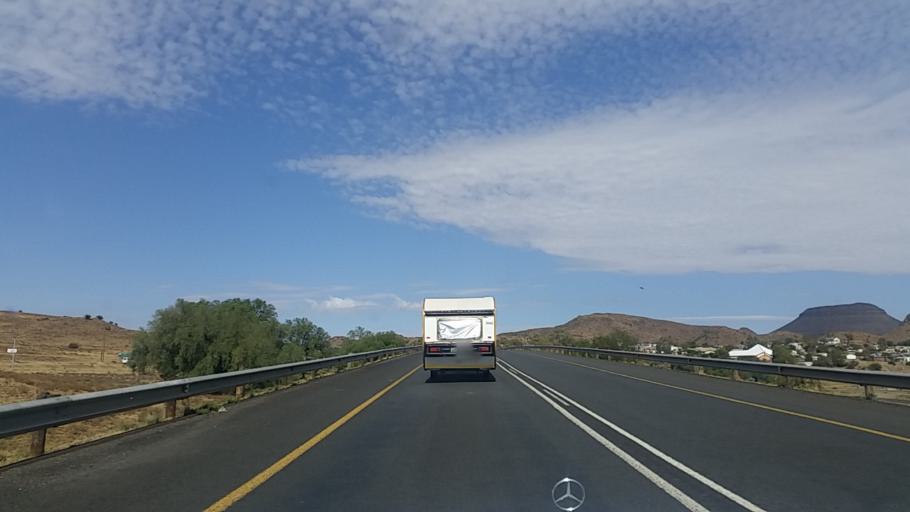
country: ZA
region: Northern Cape
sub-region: Pixley ka Seme District Municipality
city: Colesberg
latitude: -30.7089
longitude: 25.1072
